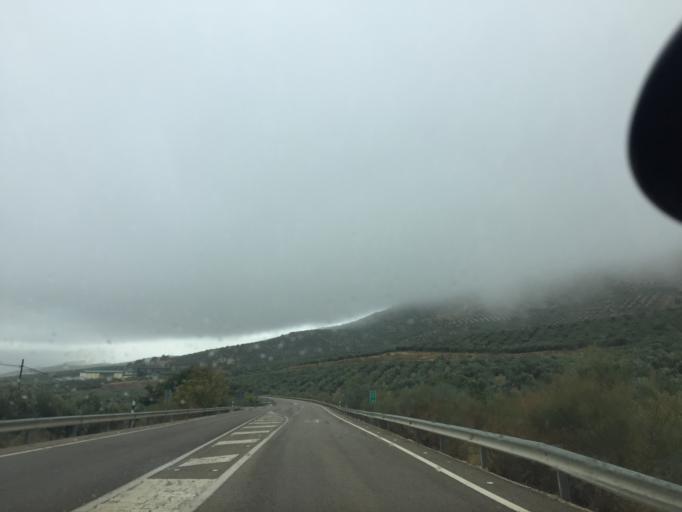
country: ES
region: Andalusia
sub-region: Provincia de Jaen
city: Jimena
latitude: 37.8472
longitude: -3.5008
